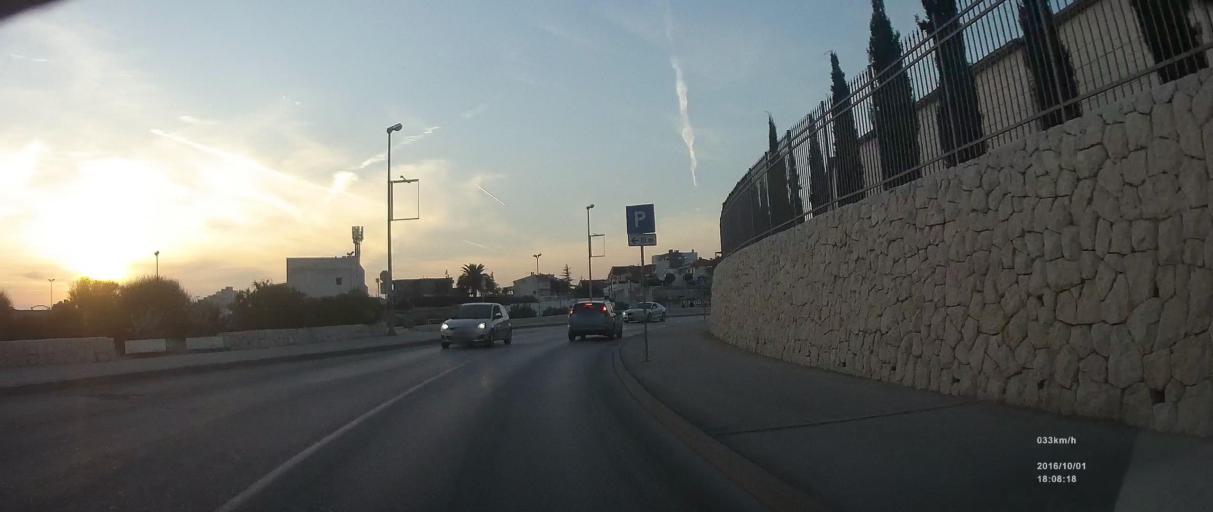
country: HR
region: Splitsko-Dalmatinska
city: Kamen
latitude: 43.5105
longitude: 16.4918
